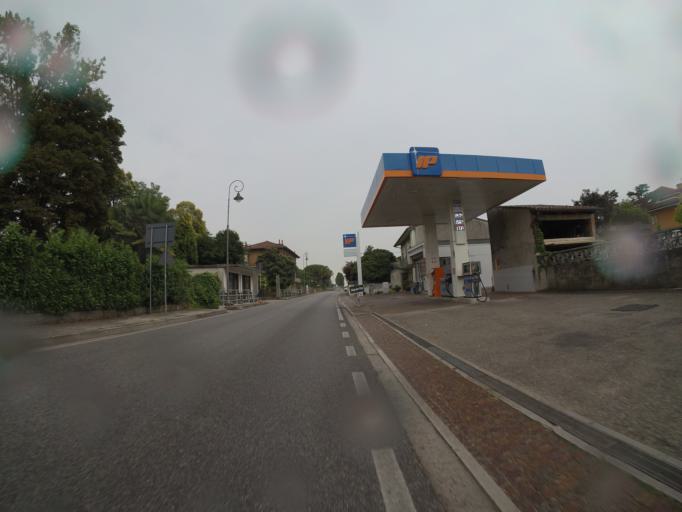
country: IT
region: Friuli Venezia Giulia
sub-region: Provincia di Udine
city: Basiliano-Vissandone
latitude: 46.0149
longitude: 13.1090
